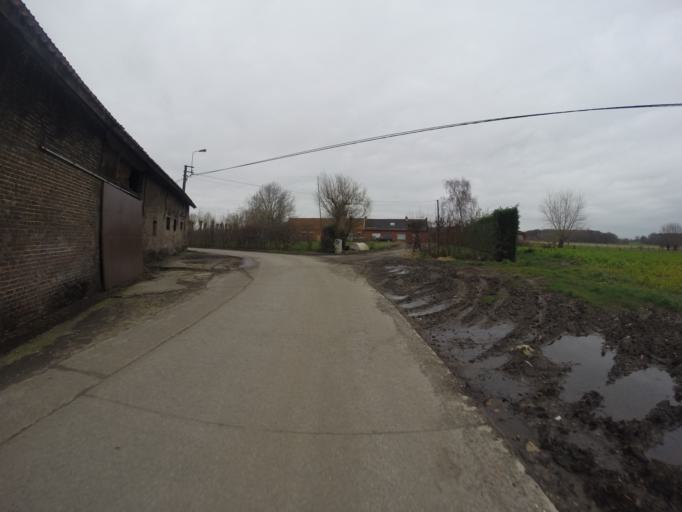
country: BE
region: Flanders
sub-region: Provincie Oost-Vlaanderen
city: Aalter
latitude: 51.1208
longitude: 3.4613
